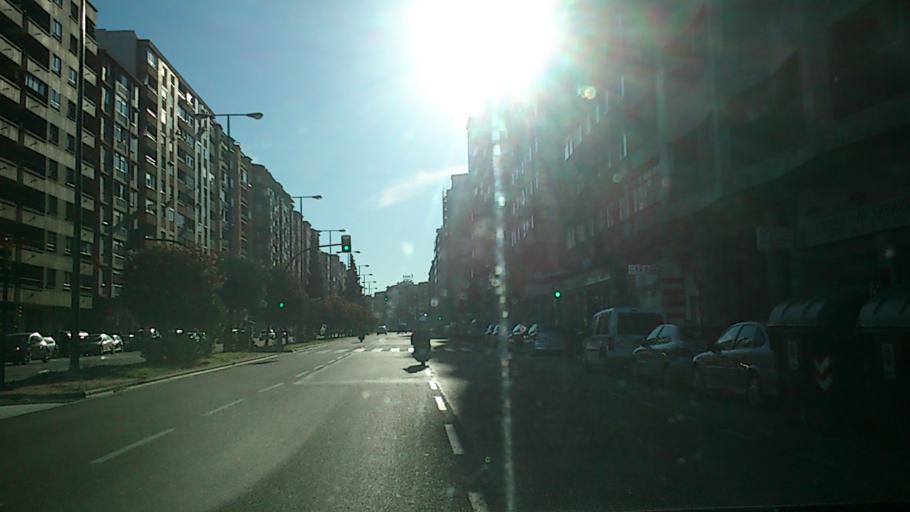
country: ES
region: Aragon
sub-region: Provincia de Zaragoza
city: Delicias
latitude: 41.6554
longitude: -0.9065
